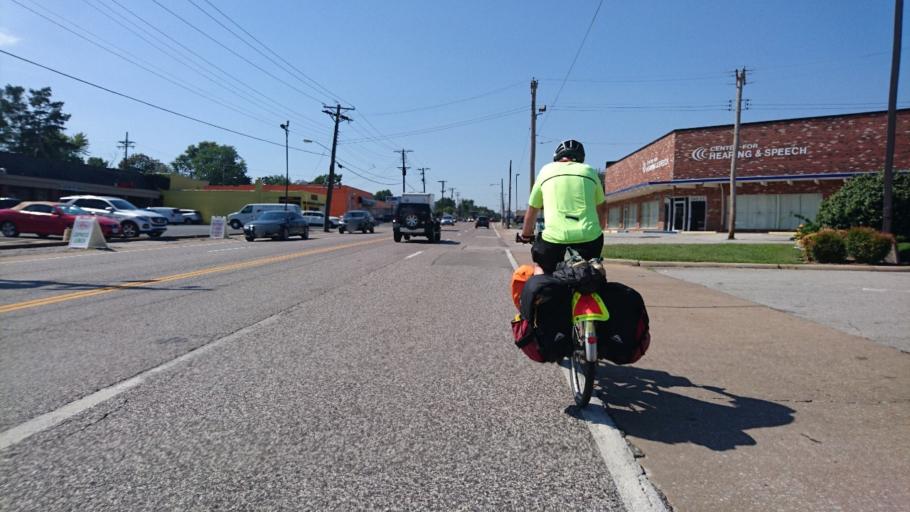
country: US
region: Missouri
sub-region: Saint Louis County
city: Rock Hill
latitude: 38.6066
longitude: -90.3747
